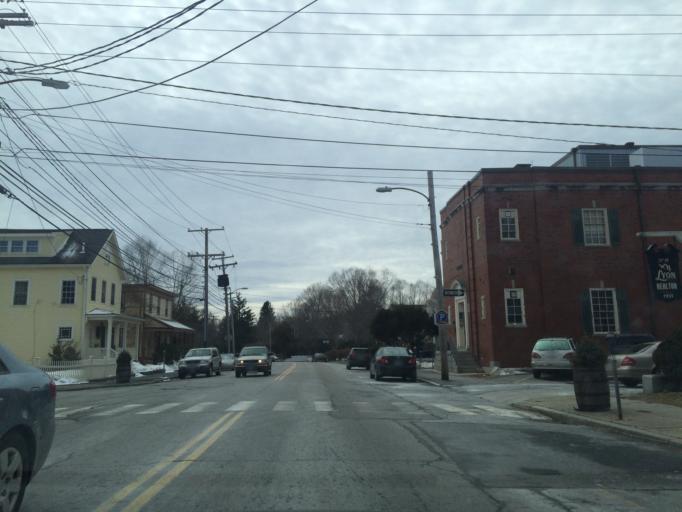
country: US
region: Massachusetts
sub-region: Middlesex County
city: Lexington
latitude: 42.4466
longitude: -71.2279
